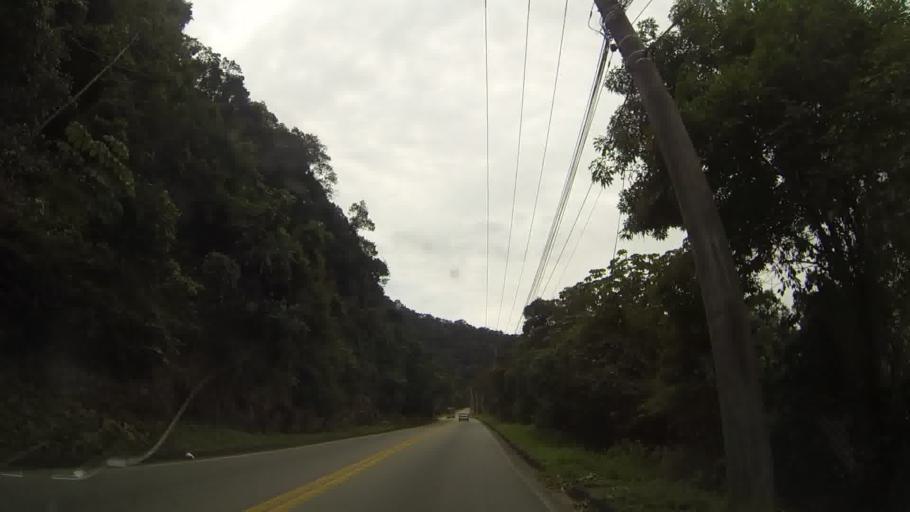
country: BR
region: Sao Paulo
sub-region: Sao Sebastiao
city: Sao Sebastiao
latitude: -23.8240
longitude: -45.4469
